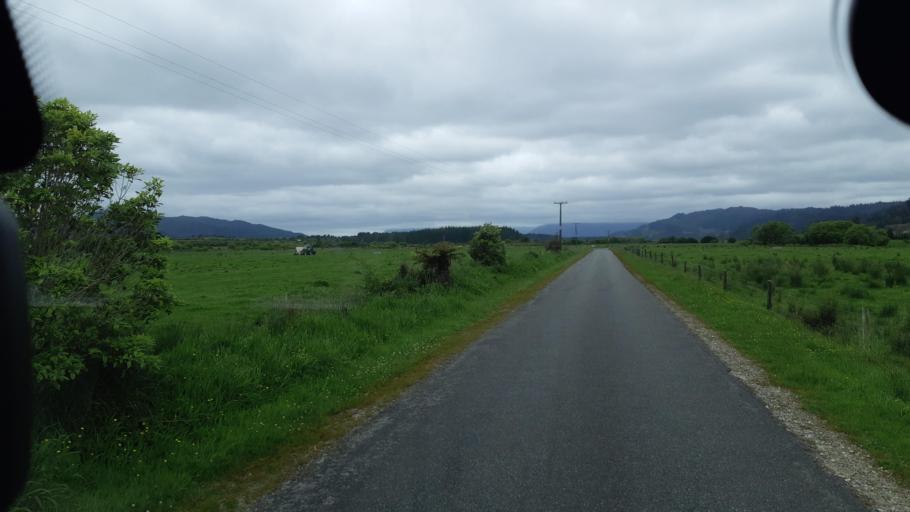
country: NZ
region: West Coast
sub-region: Westland District
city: Hokitika
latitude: -42.7093
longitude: 171.0654
